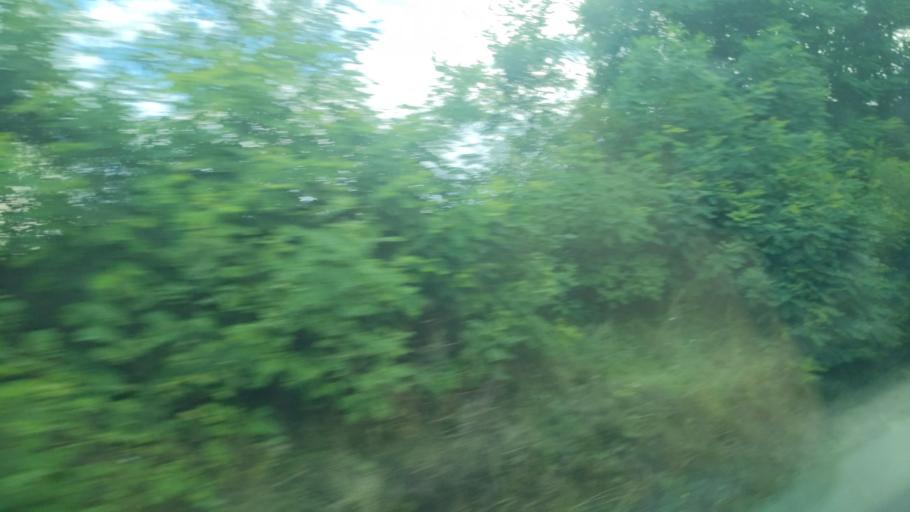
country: CZ
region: Central Bohemia
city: Cesky Brod
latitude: 50.0788
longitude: 14.8082
